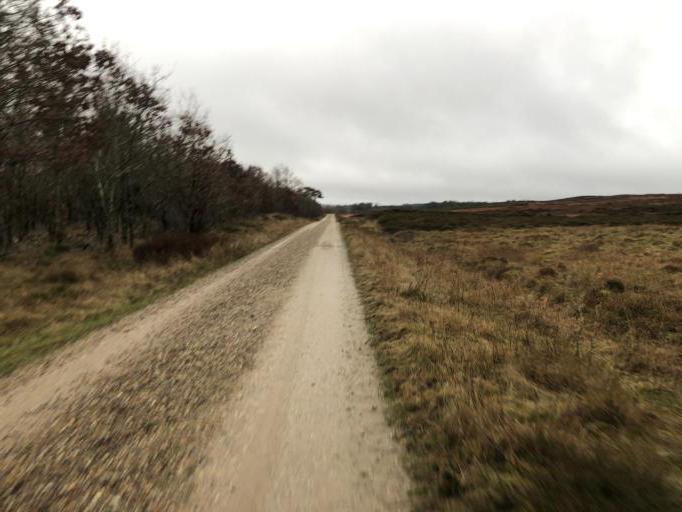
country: DK
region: Central Jutland
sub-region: Holstebro Kommune
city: Ulfborg
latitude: 56.2866
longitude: 8.4604
